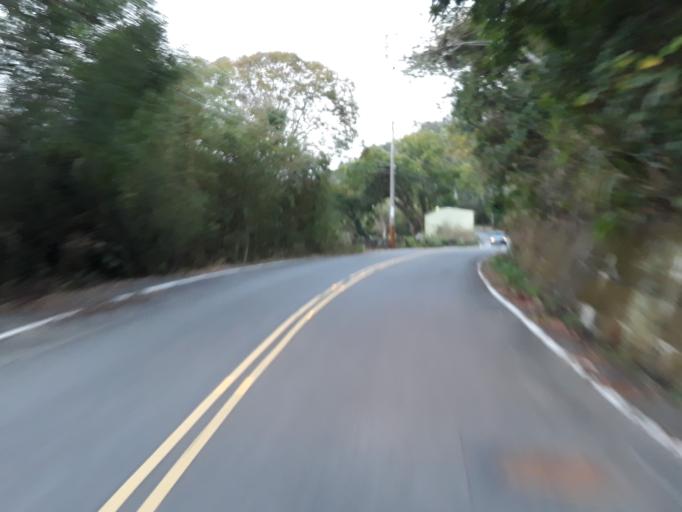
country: TW
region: Taiwan
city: Fengyuan
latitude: 24.3647
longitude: 120.8674
